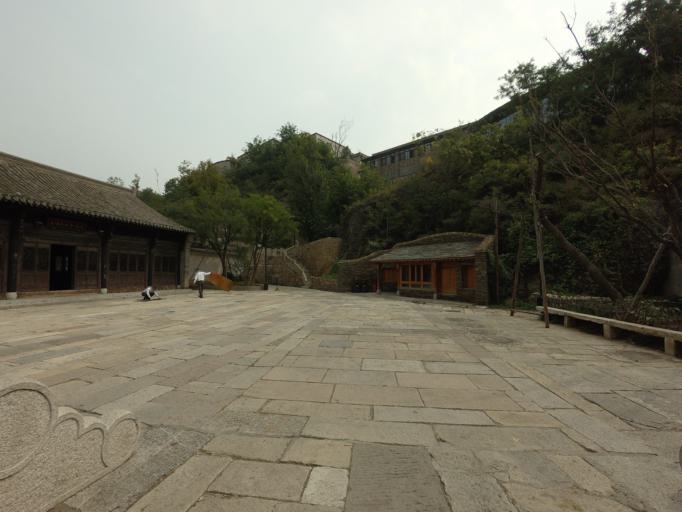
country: CN
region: Beijing
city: Xinchengzi
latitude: 40.6505
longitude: 117.2697
